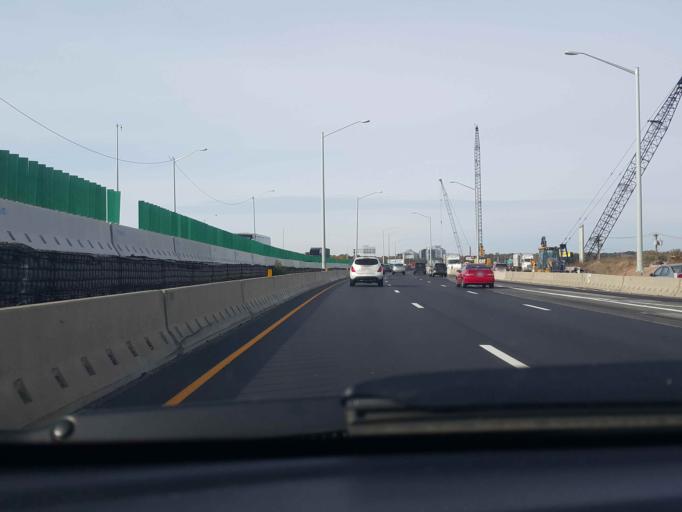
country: US
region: Connecticut
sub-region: New Haven County
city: West Haven
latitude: 41.2838
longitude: -72.9355
